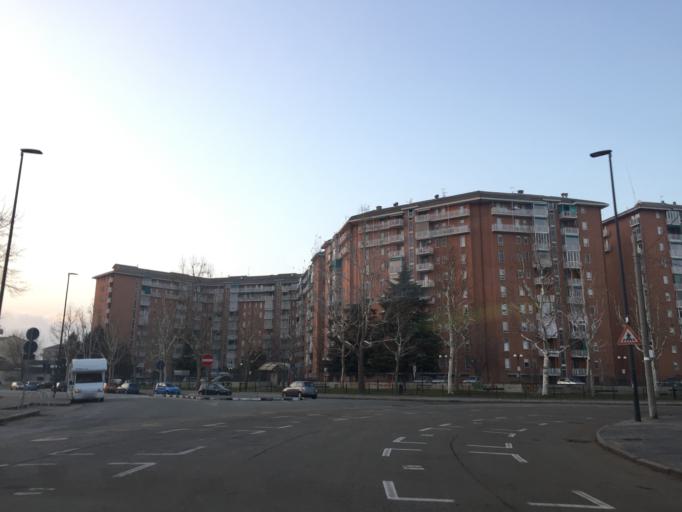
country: IT
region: Piedmont
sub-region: Provincia di Torino
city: Gerbido
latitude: 45.0436
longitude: 7.6216
